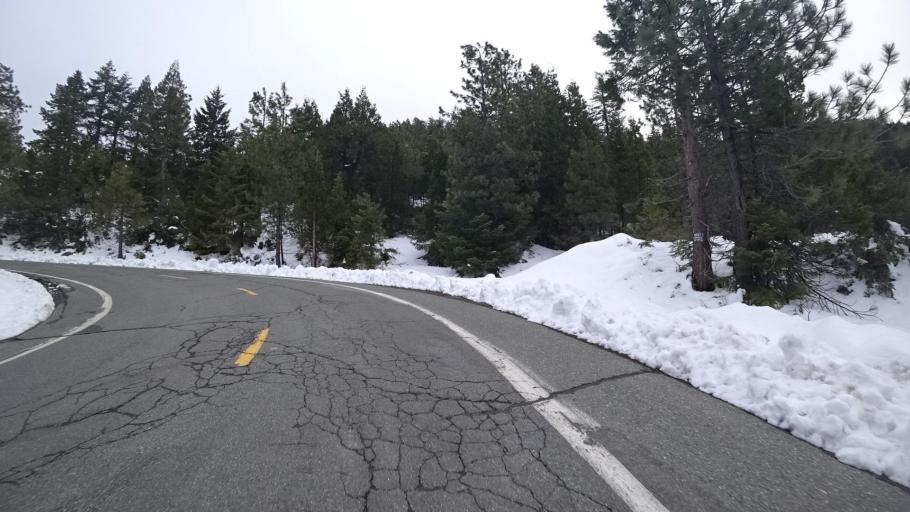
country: US
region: California
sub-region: Humboldt County
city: Willow Creek
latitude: 40.8641
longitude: -123.7390
